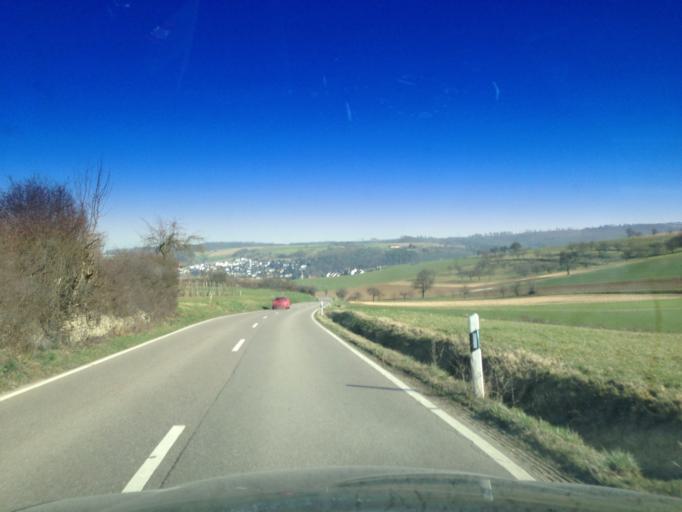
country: DE
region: Baden-Wuerttemberg
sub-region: Regierungsbezirk Stuttgart
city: Eberdingen
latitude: 48.8846
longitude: 8.9488
